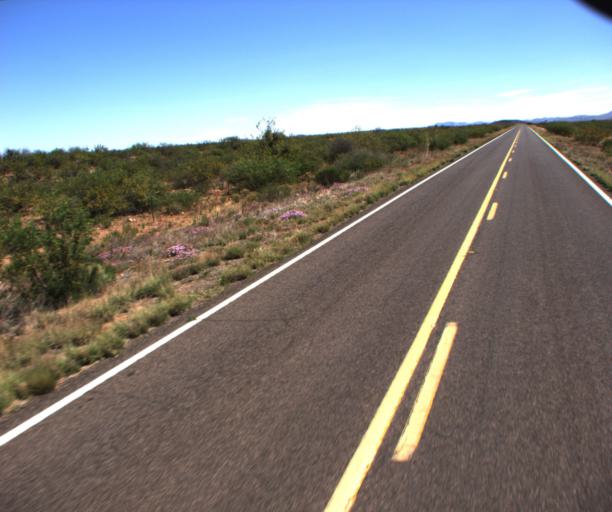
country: US
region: Arizona
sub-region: Cochise County
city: Douglas
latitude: 31.4965
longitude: -109.3318
